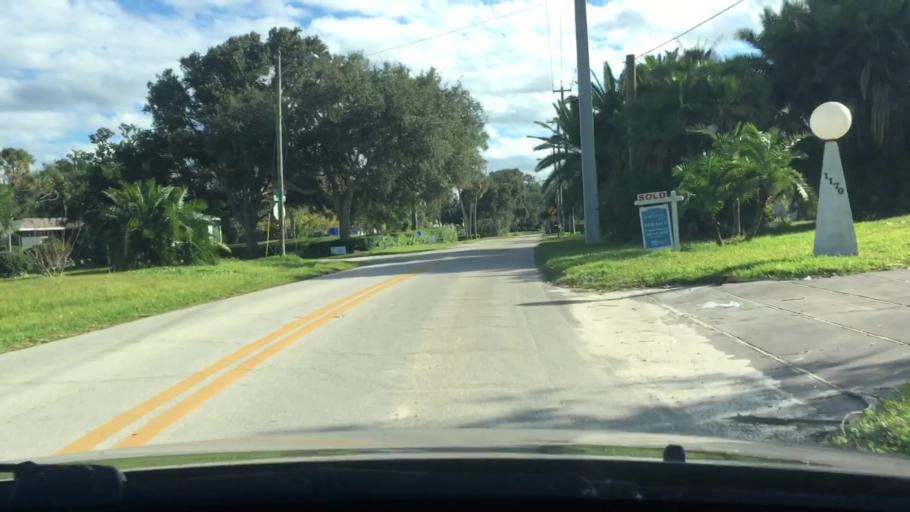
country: US
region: Florida
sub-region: Volusia County
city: Ormond-by-the-Sea
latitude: 29.3190
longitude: -81.0612
